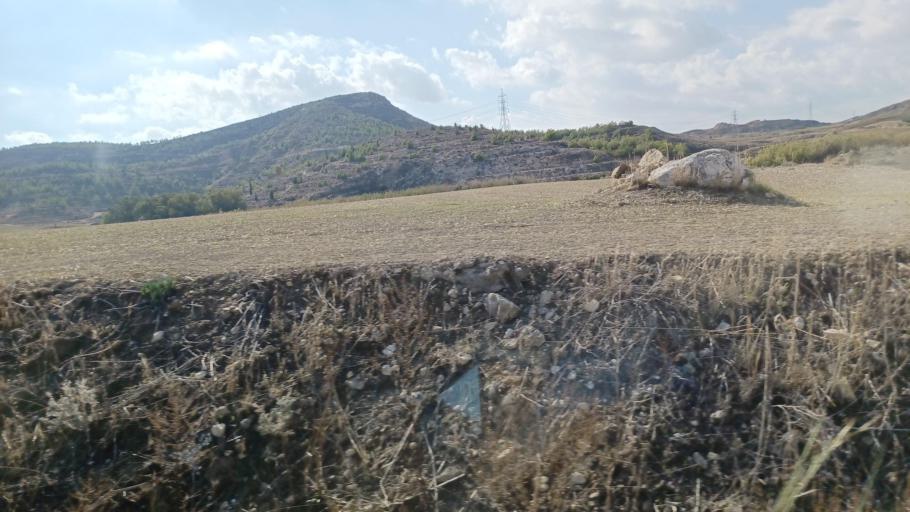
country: CY
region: Larnaka
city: Voroklini
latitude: 35.0067
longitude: 33.6480
